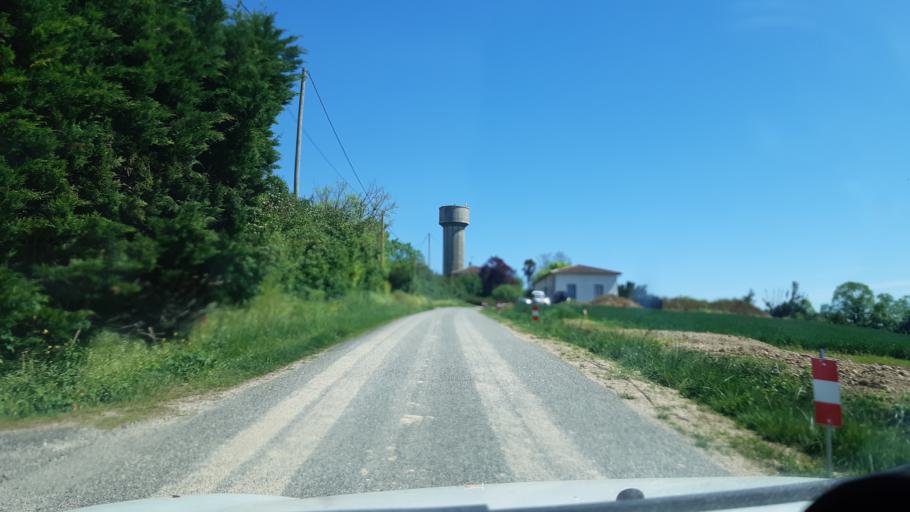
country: FR
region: Midi-Pyrenees
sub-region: Departement du Gers
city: Samatan
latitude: 43.5142
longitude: 1.0010
